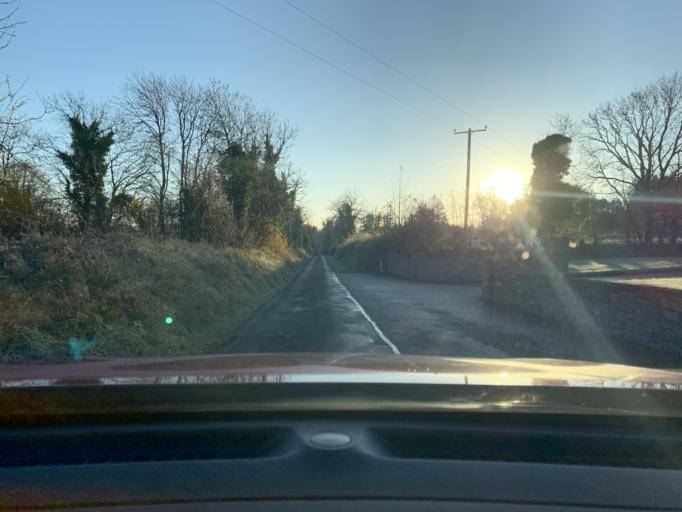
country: IE
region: Connaught
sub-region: Sligo
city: Ballymote
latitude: 53.9860
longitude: -8.5217
